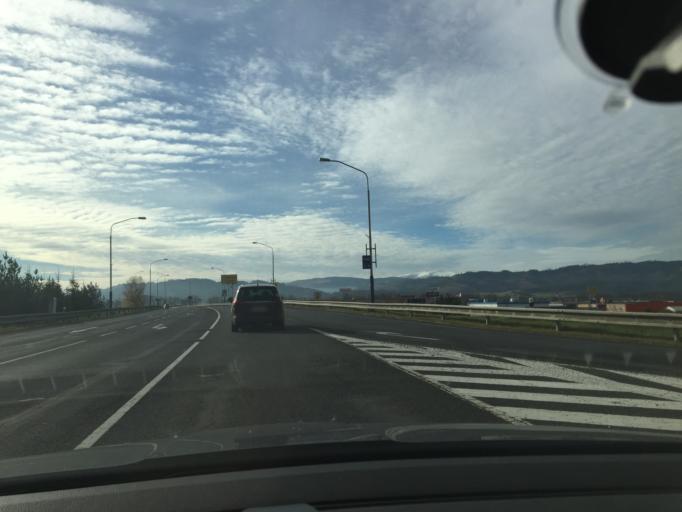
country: SK
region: Presovsky
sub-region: Okres Poprad
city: Poprad
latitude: 49.0647
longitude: 20.2689
